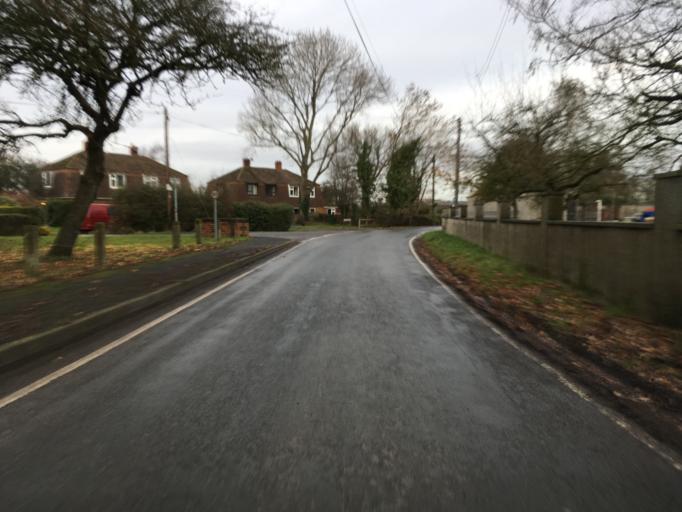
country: GB
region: Wales
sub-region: Newport
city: Redwick
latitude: 51.5547
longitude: -2.8477
